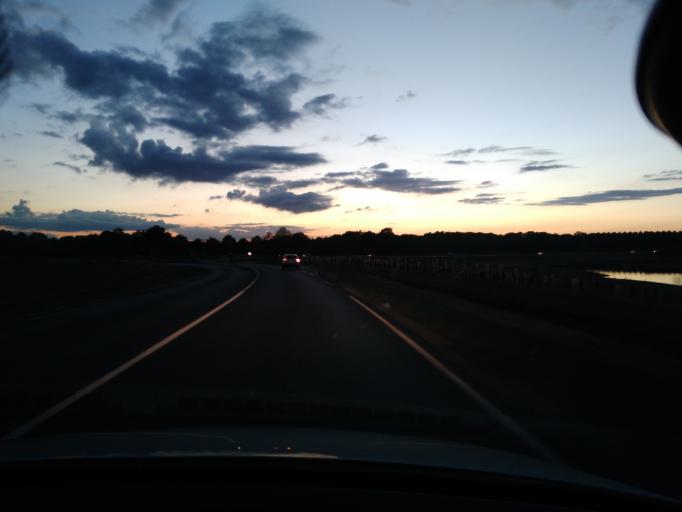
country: FR
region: Ile-de-France
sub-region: Departement de Seine-et-Marne
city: Villeneuve-le-Comte
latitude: 48.8196
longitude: 2.8211
